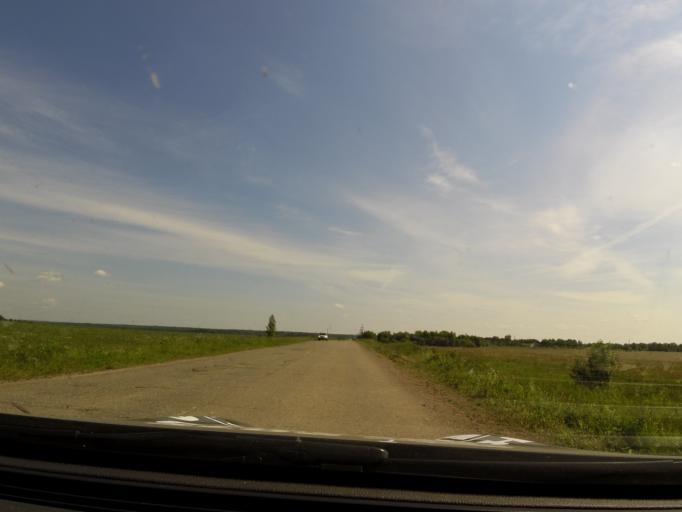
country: RU
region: Kostroma
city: Galich
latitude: 58.4451
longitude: 42.2944
